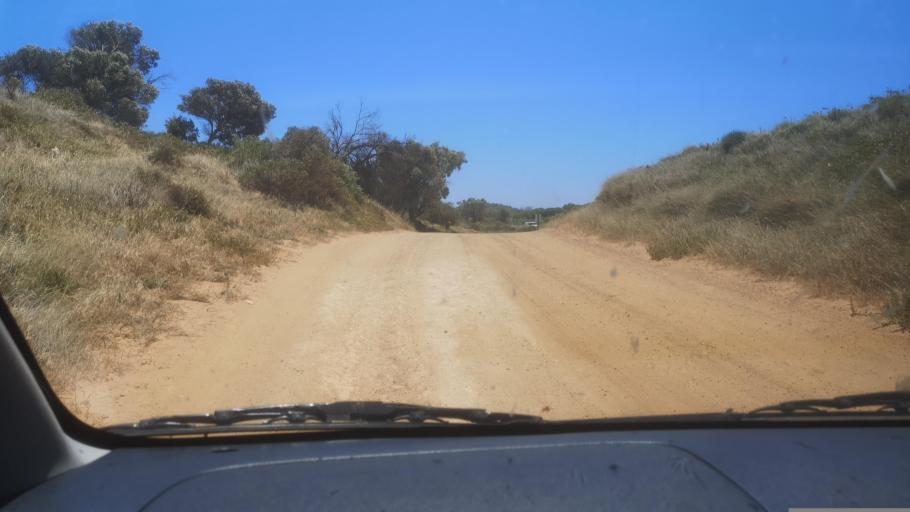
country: AU
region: Western Australia
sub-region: Dandaragan
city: Jurien Bay
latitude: -30.1830
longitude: 114.9992
